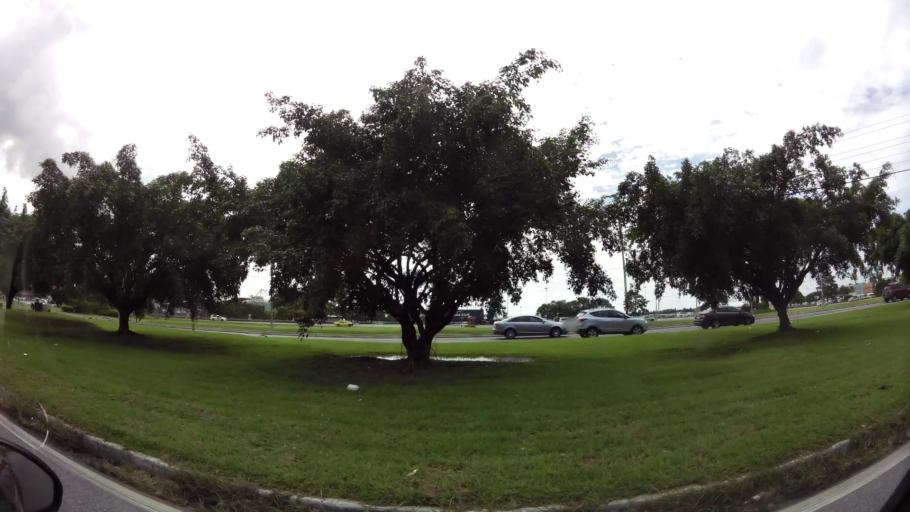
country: TT
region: City of Port of Spain
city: Mucurapo
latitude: 10.6606
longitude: -61.5297
